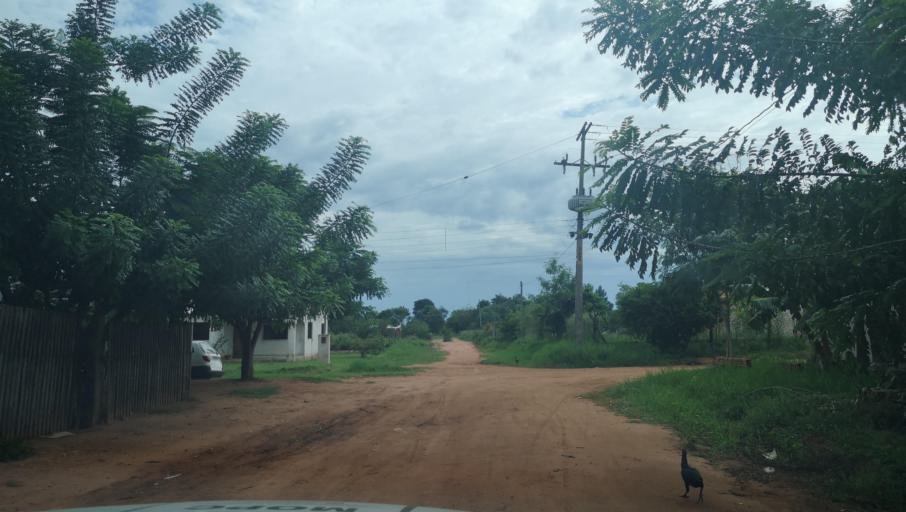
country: PY
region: San Pedro
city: Capiibary
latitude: -24.7251
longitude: -56.0213
